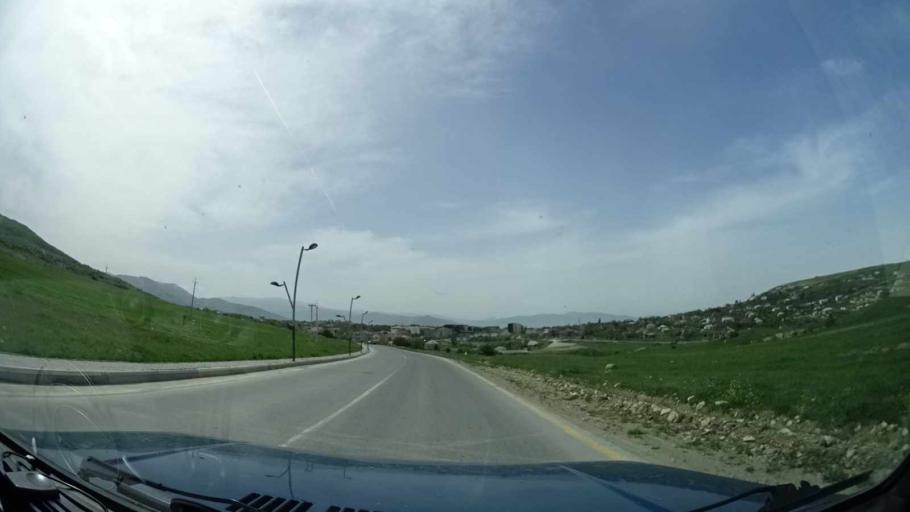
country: AZ
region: Xizi
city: Khyzy
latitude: 40.9098
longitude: 49.0800
